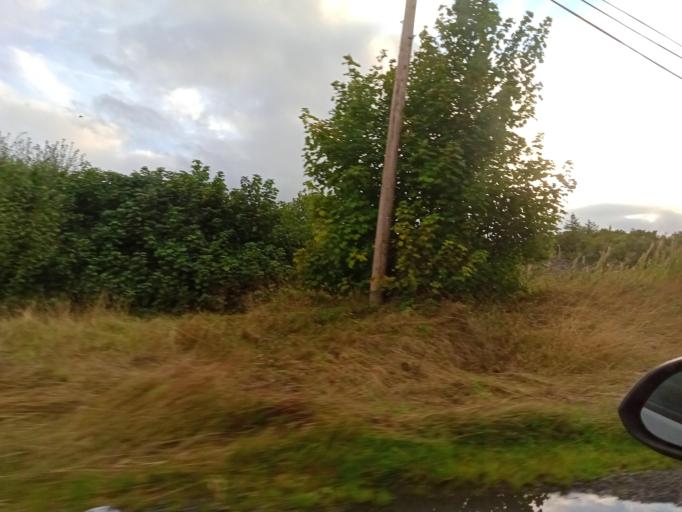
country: IE
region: Leinster
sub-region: Uibh Fhaili
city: Tullamore
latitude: 53.1461
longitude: -7.4827
